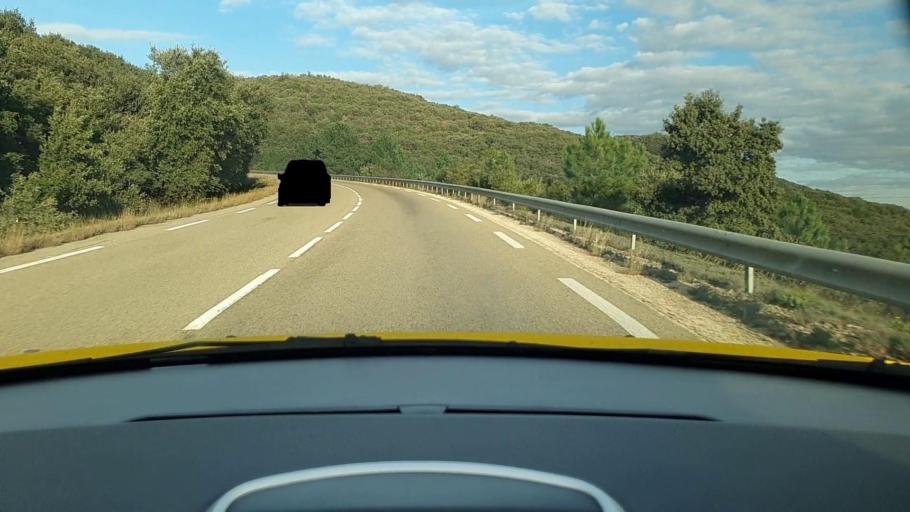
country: FR
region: Languedoc-Roussillon
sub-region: Departement du Gard
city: Laval-Pradel
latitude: 44.2116
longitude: 4.0943
